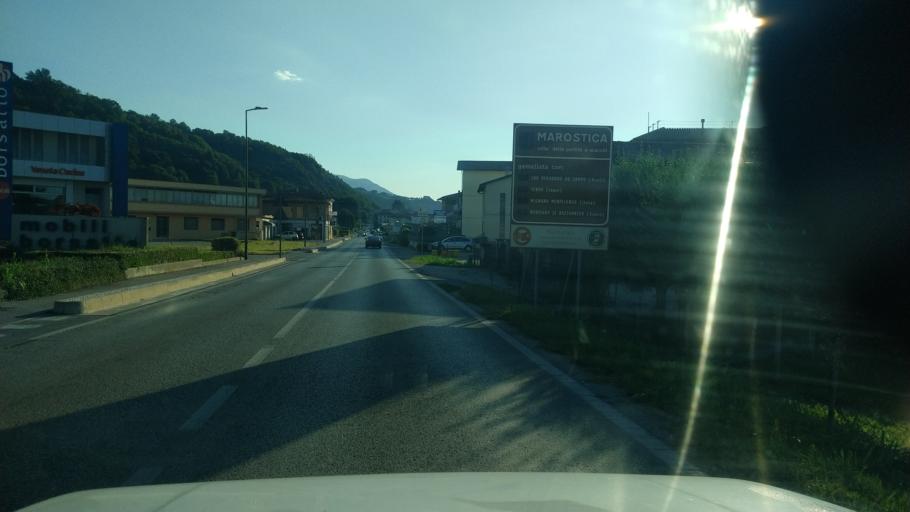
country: IT
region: Veneto
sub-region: Provincia di Vicenza
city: Pianezze
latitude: 45.7384
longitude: 11.6408
